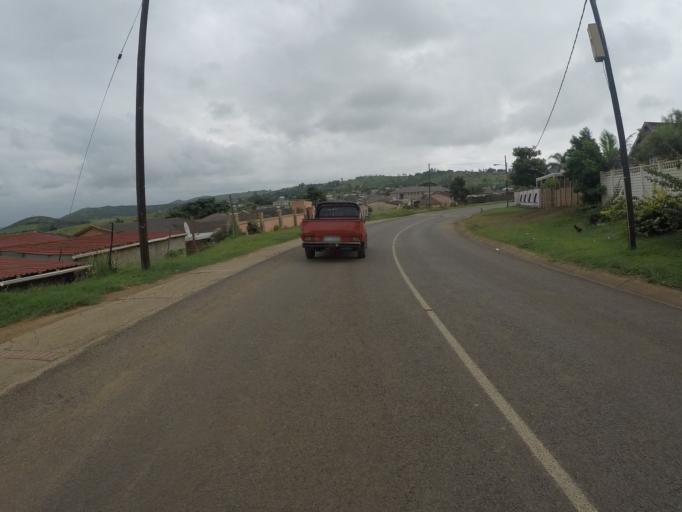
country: ZA
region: KwaZulu-Natal
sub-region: uThungulu District Municipality
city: Empangeni
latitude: -28.7768
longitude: 31.8479
